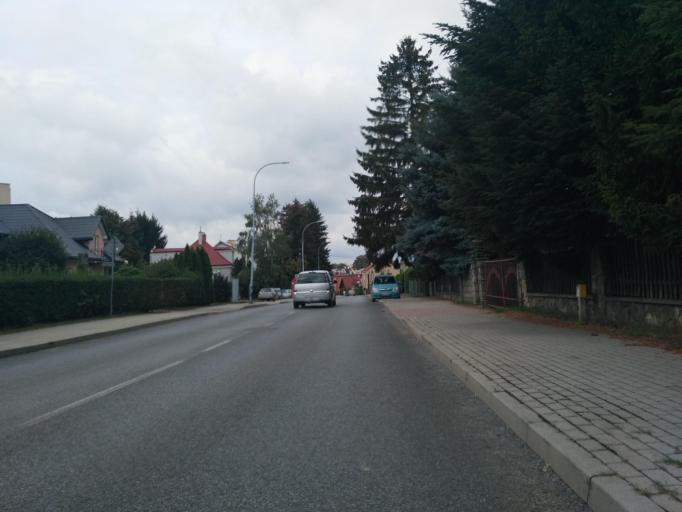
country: PL
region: Subcarpathian Voivodeship
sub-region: Krosno
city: Krosno
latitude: 49.6884
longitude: 21.7809
